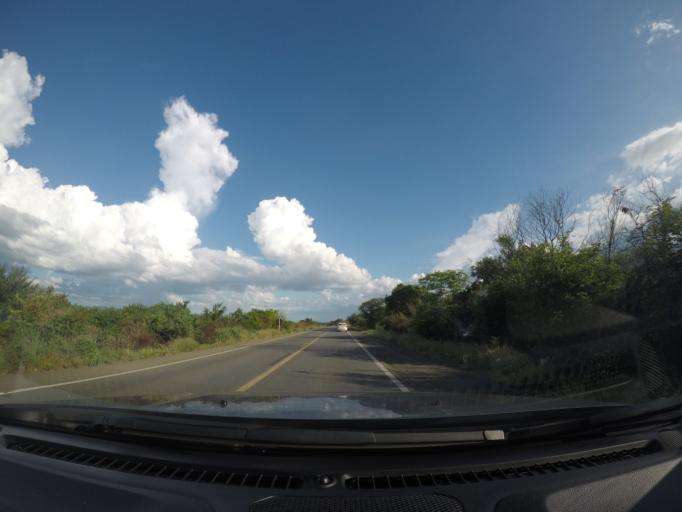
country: BR
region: Bahia
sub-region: Oliveira Dos Brejinhos
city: Oliveira dos Brejinhos
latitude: -12.0824
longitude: -42.9417
